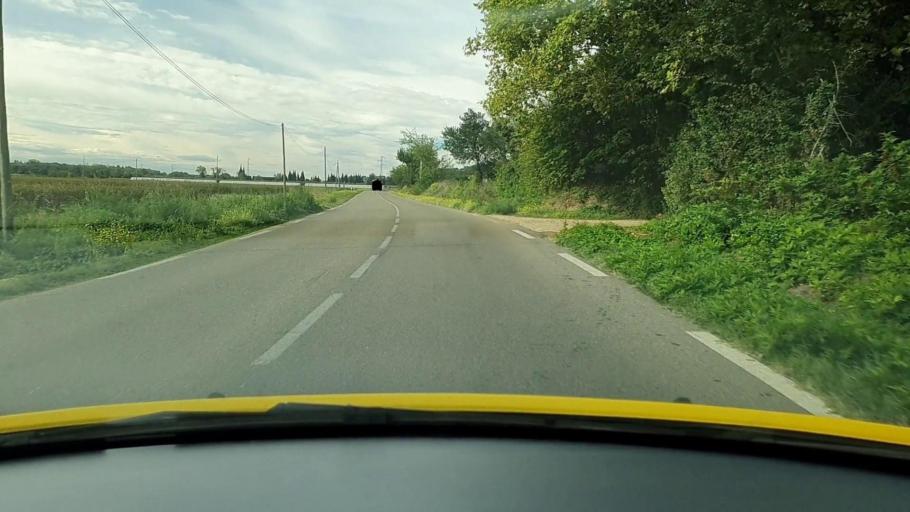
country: FR
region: Languedoc-Roussillon
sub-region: Departement du Gard
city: Bellegarde
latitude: 43.7777
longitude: 4.5438
